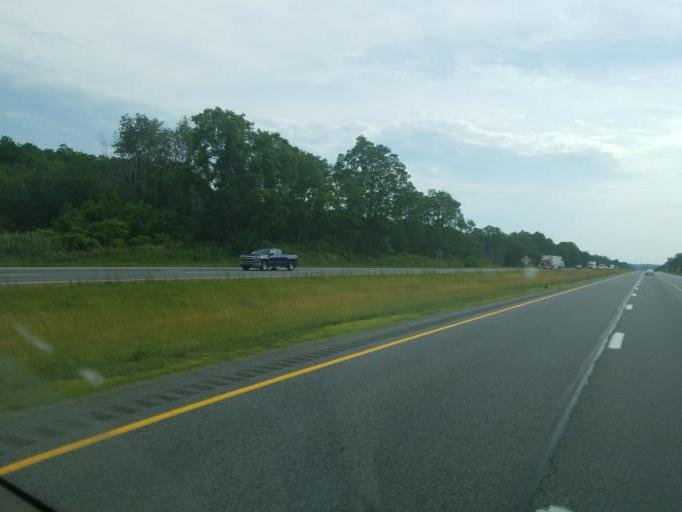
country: US
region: Pennsylvania
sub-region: Erie County
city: Northwest Harborcreek
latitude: 42.1488
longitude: -79.9033
